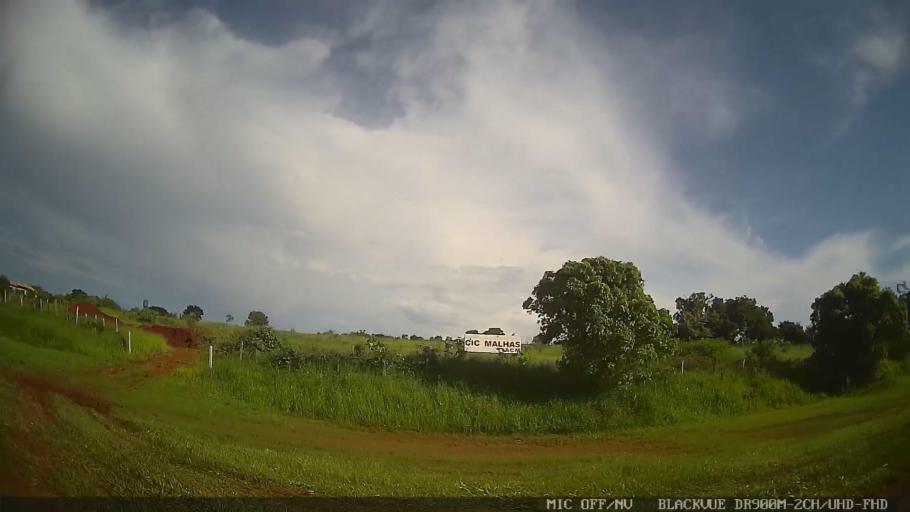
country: BR
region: Sao Paulo
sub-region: Tiete
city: Tiete
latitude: -23.0876
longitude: -47.6809
